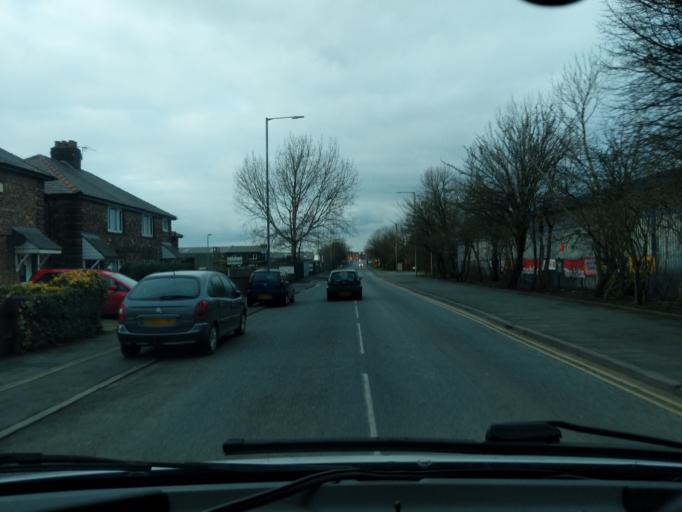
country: GB
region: England
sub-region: St. Helens
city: St Helens
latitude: 53.4458
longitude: -2.7192
